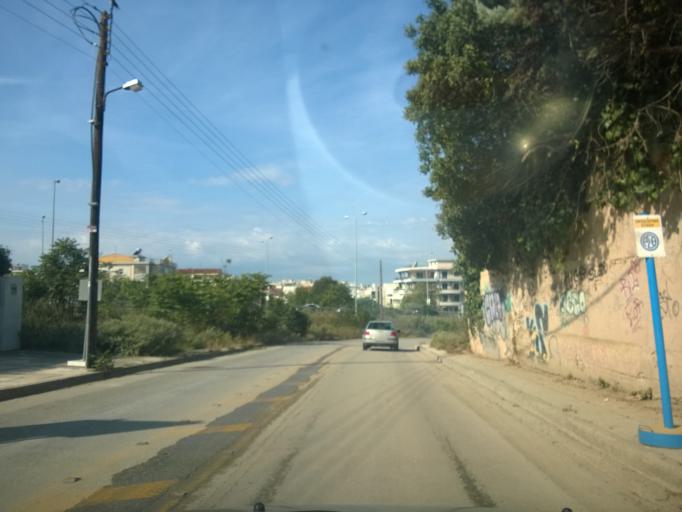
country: GR
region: Central Macedonia
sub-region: Nomos Thessalonikis
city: Pylaia
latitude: 40.5883
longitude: 22.9706
